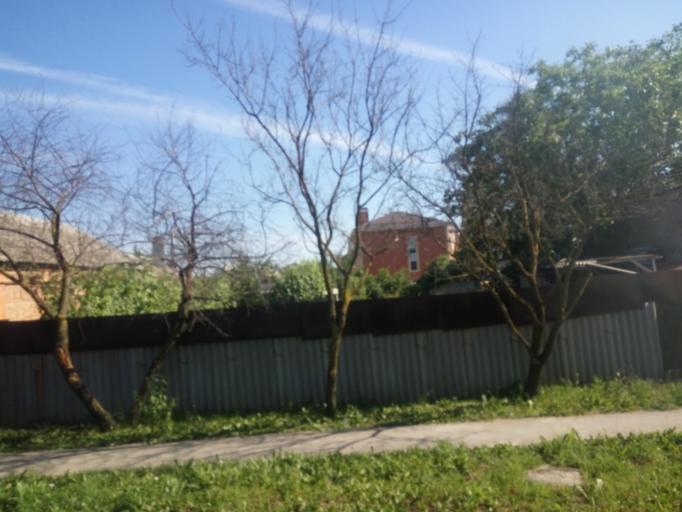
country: RU
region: Rostov
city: Bataysk
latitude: 47.1208
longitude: 39.7359
